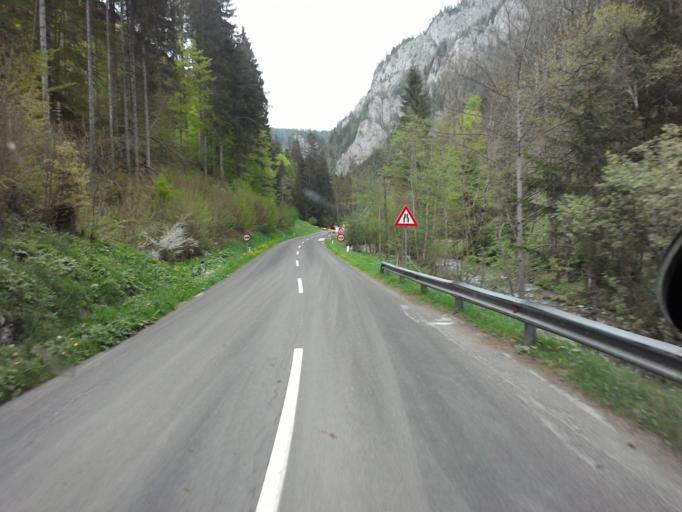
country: AT
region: Styria
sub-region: Politischer Bezirk Liezen
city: Sankt Gallen
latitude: 47.6789
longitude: 14.5101
